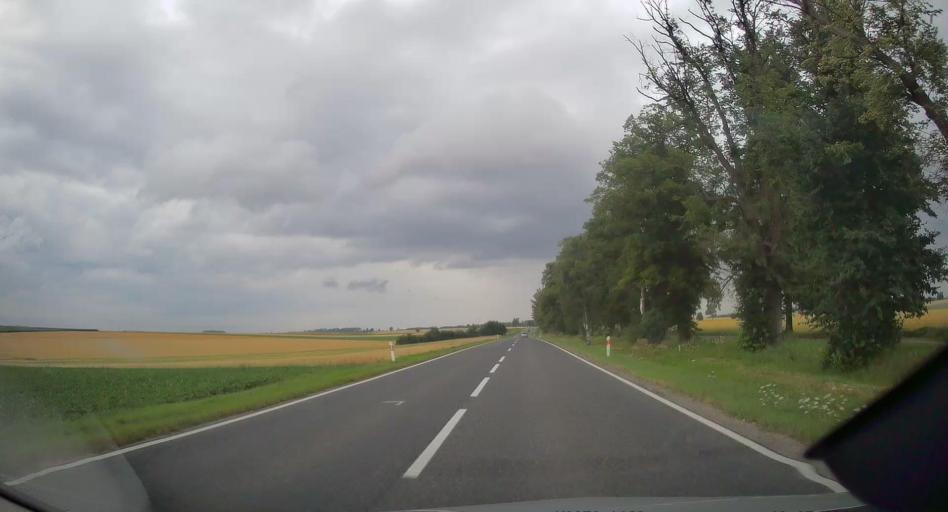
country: PL
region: Opole Voivodeship
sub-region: Powiat prudnicki
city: Laka Prudnicka
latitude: 50.4151
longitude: 17.4897
